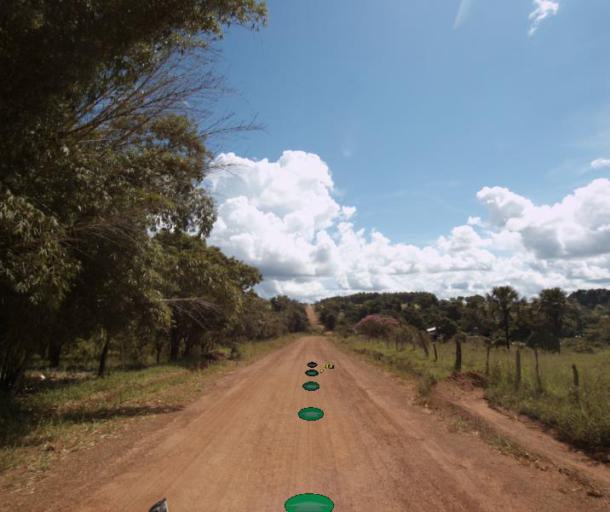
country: BR
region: Goias
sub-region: Pirenopolis
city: Pirenopolis
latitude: -15.7812
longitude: -48.8149
